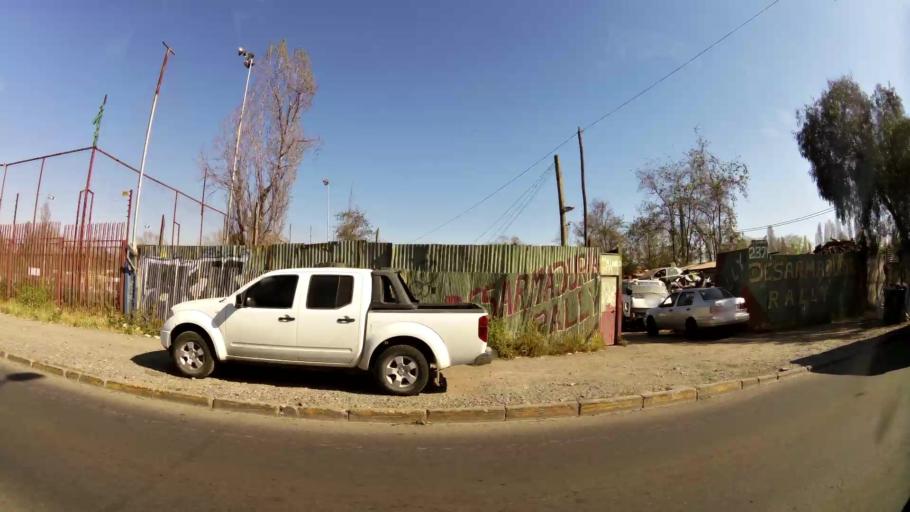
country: CL
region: Santiago Metropolitan
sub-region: Provincia de Santiago
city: La Pintana
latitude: -33.5880
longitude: -70.6367
